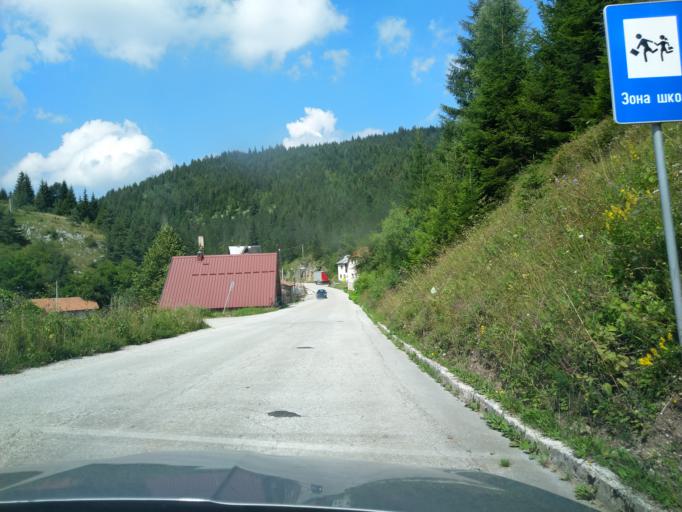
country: RS
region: Central Serbia
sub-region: Zlatiborski Okrug
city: Nova Varos
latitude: 43.5458
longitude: 19.9023
